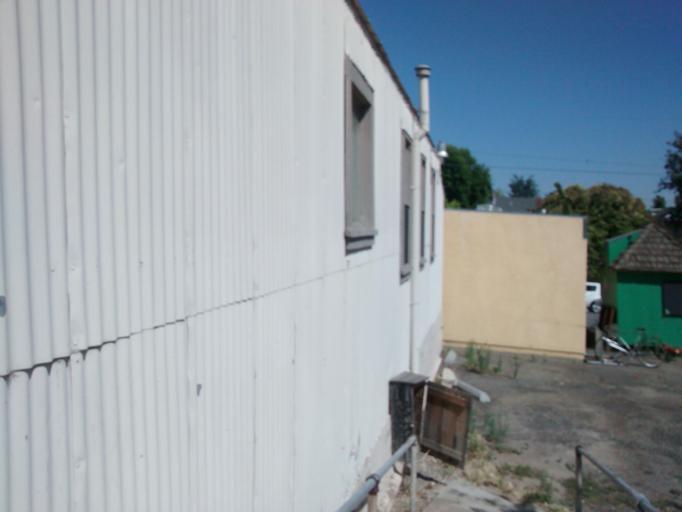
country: US
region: California
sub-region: San Luis Obispo County
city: San Luis Obispo
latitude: 35.2756
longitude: -120.6555
